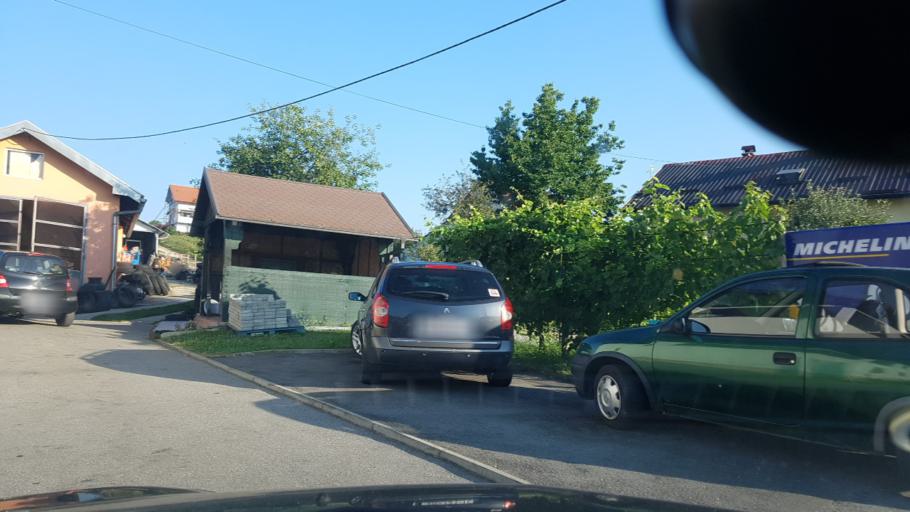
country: HR
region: Krapinsko-Zagorska
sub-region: Grad Krapina
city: Krapina
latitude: 46.1359
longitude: 15.8874
